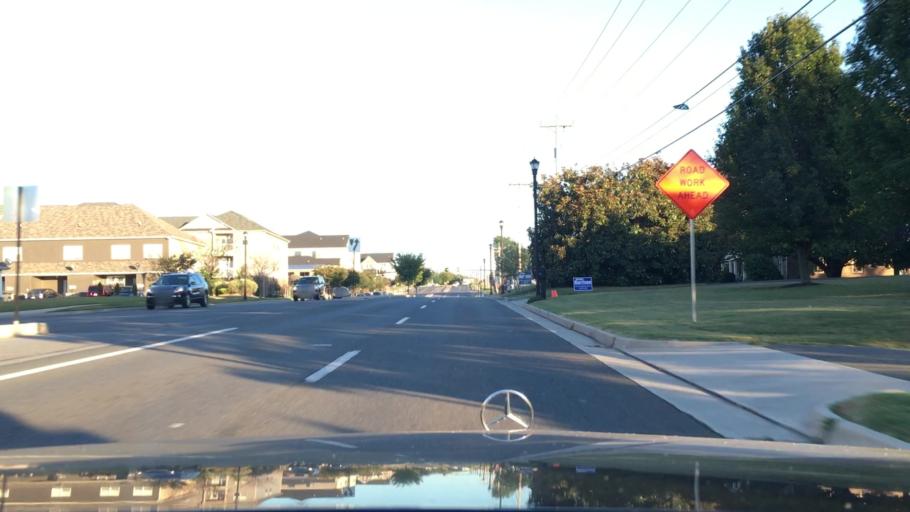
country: US
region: Virginia
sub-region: Campbell County
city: Timberlake
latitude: 37.3404
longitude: -79.2279
